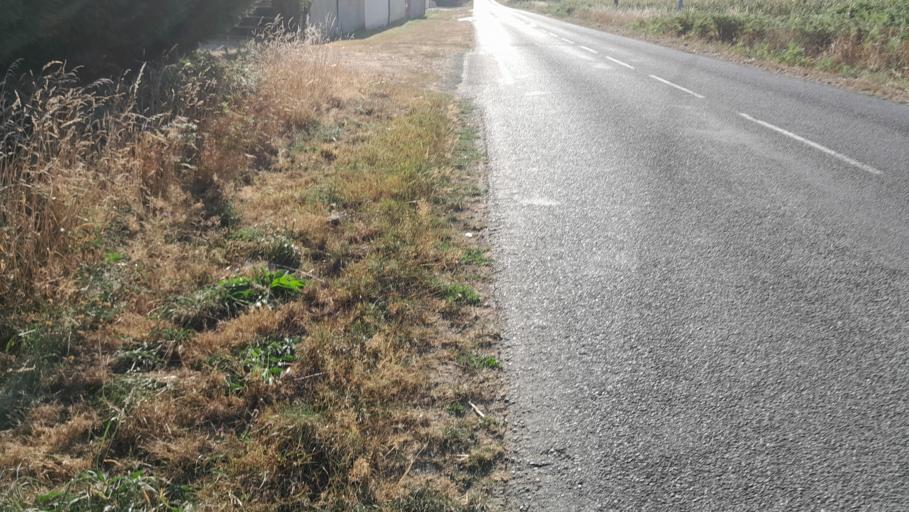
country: FR
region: Brittany
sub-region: Departement d'Ille-et-Vilaine
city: Le Pertre
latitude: 47.9667
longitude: -1.0613
